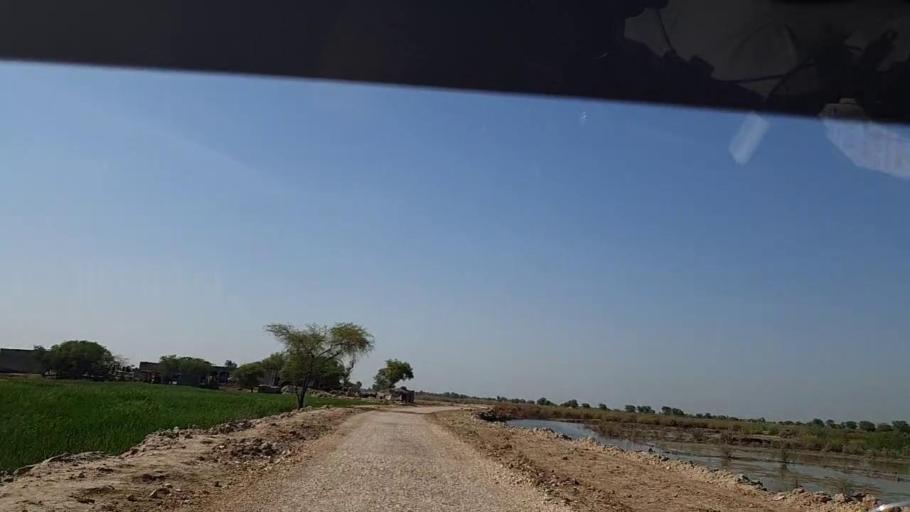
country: PK
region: Sindh
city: Tangwani
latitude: 28.3267
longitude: 69.0798
